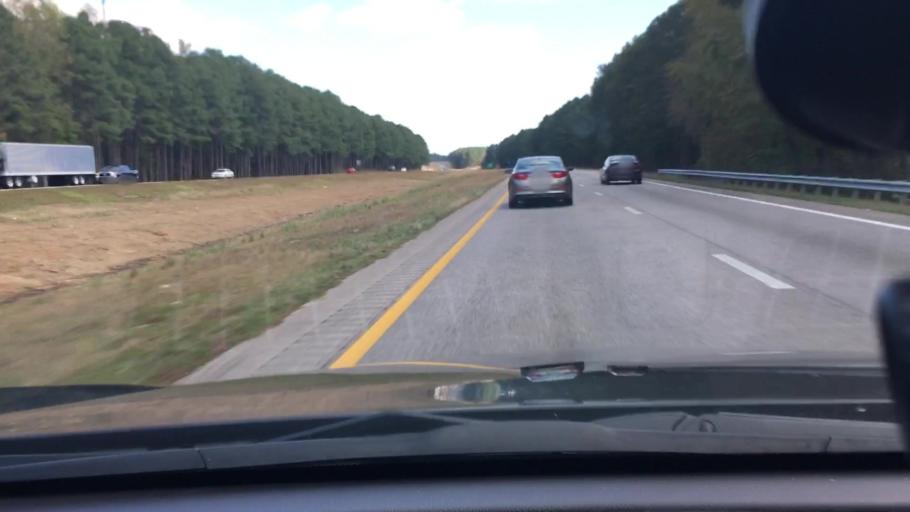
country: US
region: North Carolina
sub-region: Nash County
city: Spring Hope
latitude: 35.7885
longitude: -78.1330
